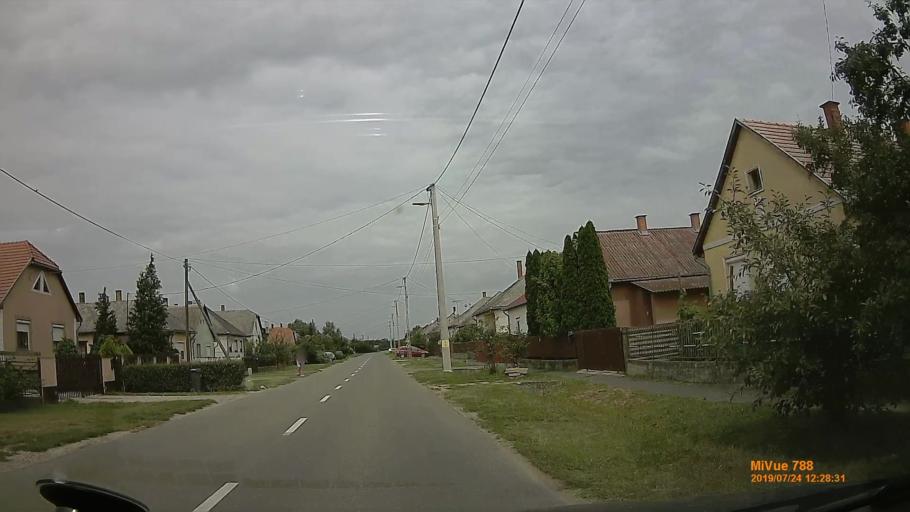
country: HU
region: Szabolcs-Szatmar-Bereg
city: Vasarosnameny
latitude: 48.1426
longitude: 22.3453
